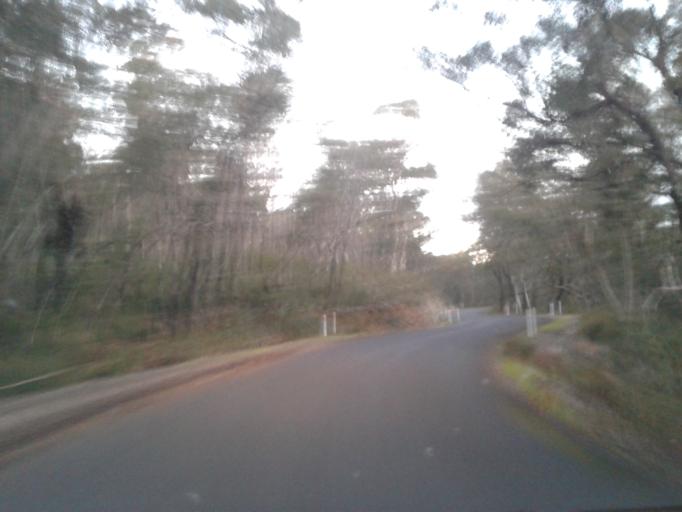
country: AU
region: Victoria
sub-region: Northern Grampians
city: Stawell
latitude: -37.1636
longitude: 142.4952
